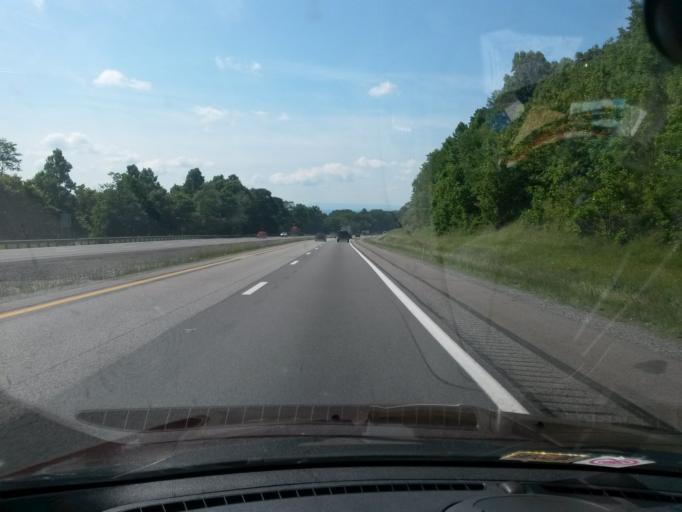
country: US
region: West Virginia
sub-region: Raleigh County
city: Shady Spring
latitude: 37.5732
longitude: -81.1140
